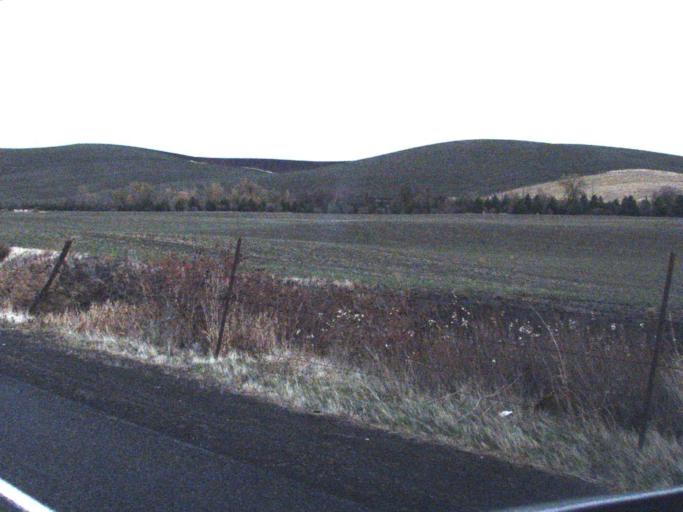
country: US
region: Washington
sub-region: Walla Walla County
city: Waitsburg
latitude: 46.2254
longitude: -118.1376
